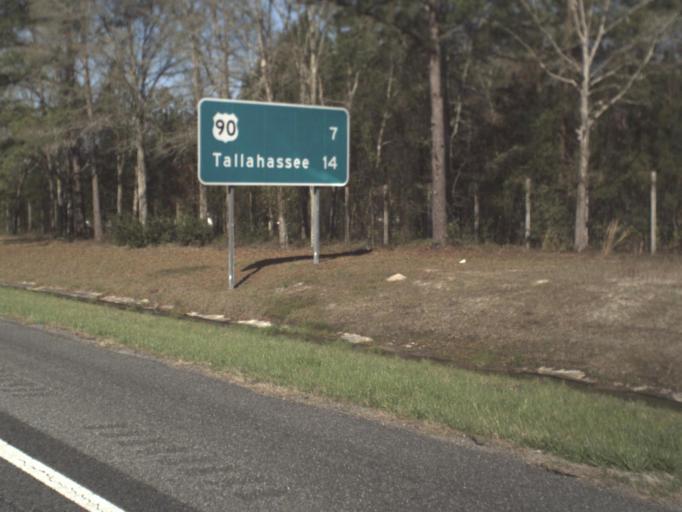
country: US
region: Florida
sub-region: Jefferson County
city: Monticello
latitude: 30.4835
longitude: -84.0431
